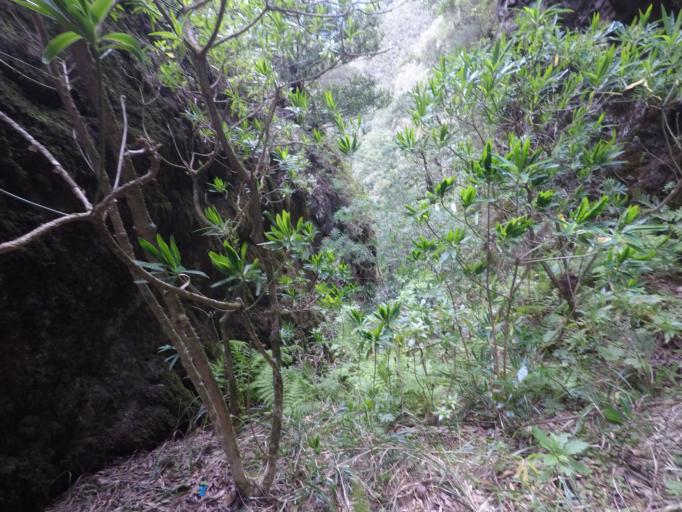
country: PT
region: Madeira
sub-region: Camara de Lobos
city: Curral das Freiras
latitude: 32.7699
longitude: -16.9752
